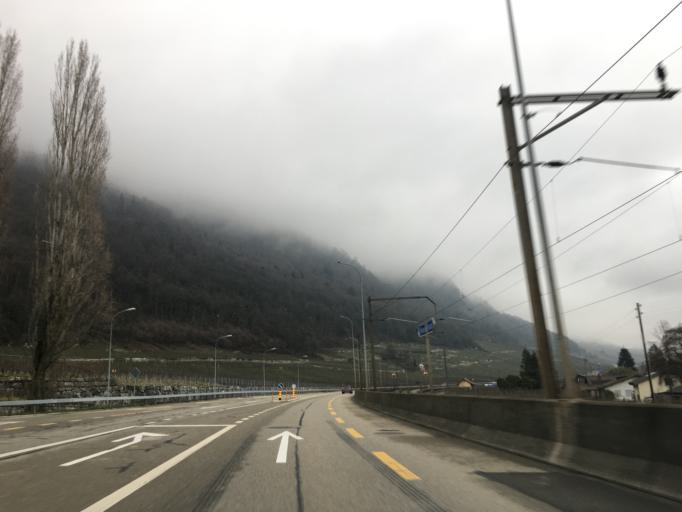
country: CH
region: Bern
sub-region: Jura bernois
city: La Neuveville
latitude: 47.0738
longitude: 7.1133
